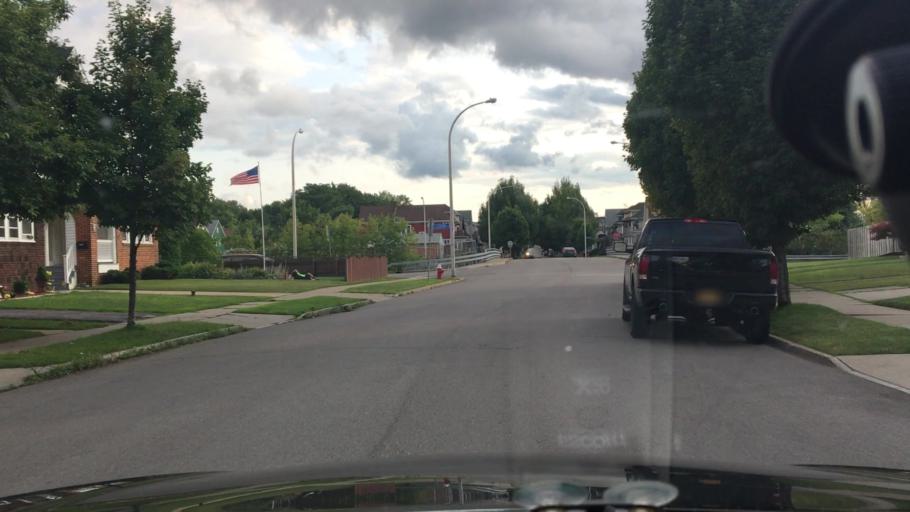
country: US
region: New York
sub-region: Erie County
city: West Seneca
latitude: 42.8571
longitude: -78.8156
